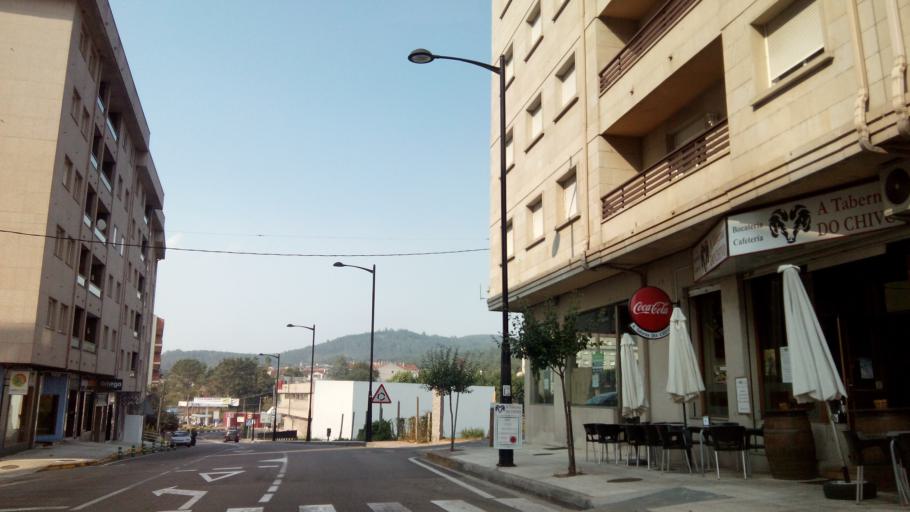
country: ES
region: Galicia
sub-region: Provincia de Pontevedra
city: Ponteareas
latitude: 42.1758
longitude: -8.5089
